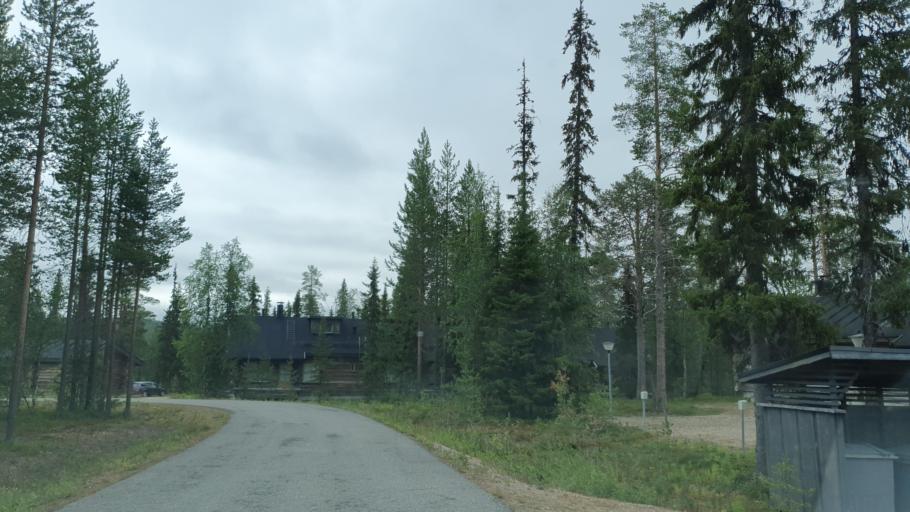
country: FI
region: Lapland
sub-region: Tunturi-Lappi
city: Kolari
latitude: 67.6009
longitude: 24.1780
